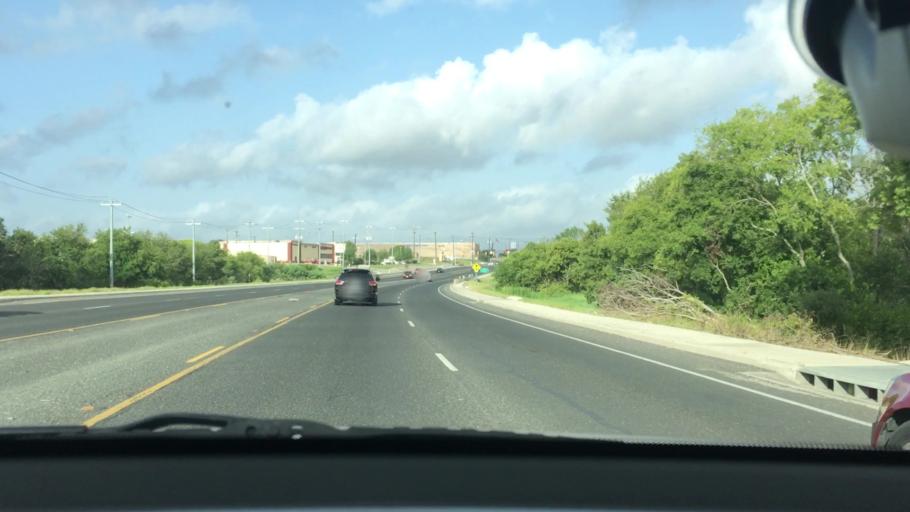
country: US
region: Texas
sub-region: Bexar County
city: Converse
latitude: 29.4868
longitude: -98.3438
